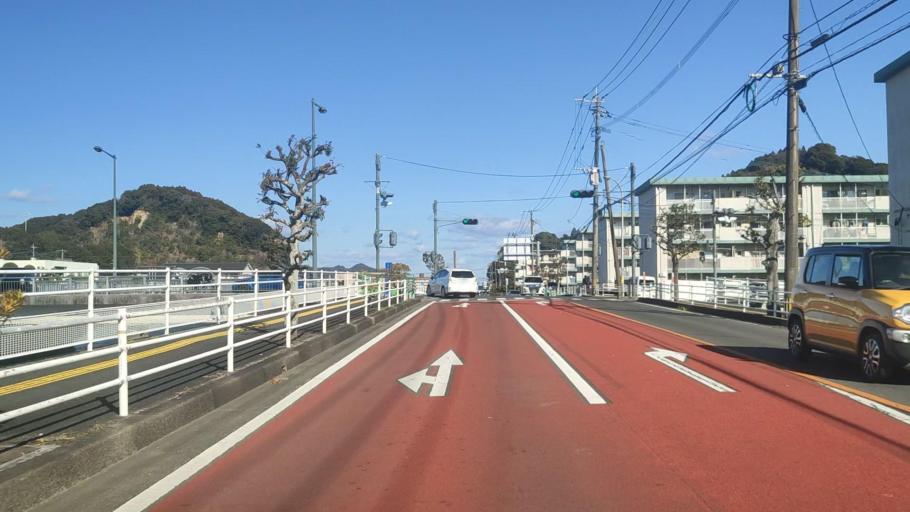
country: JP
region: Oita
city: Saiki
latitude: 32.9554
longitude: 131.9088
